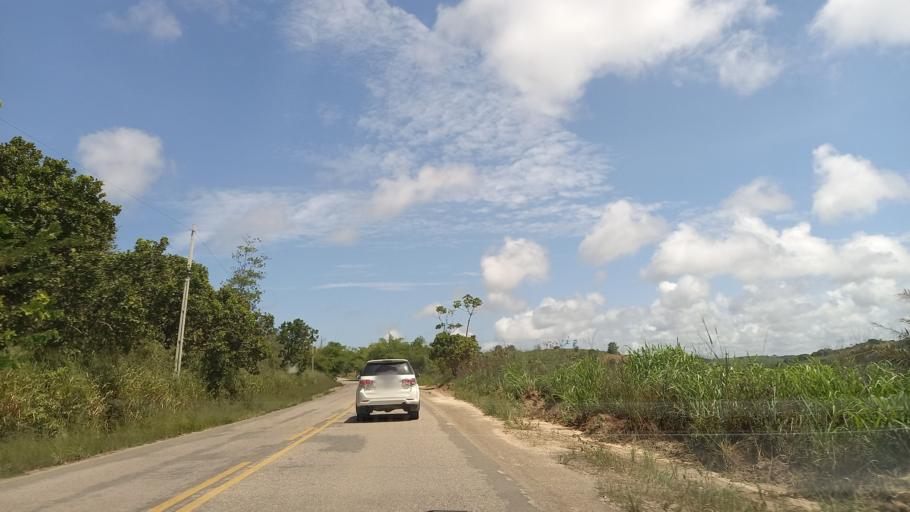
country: BR
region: Pernambuco
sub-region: Barreiros
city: Barreiros
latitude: -8.8507
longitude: -35.1670
